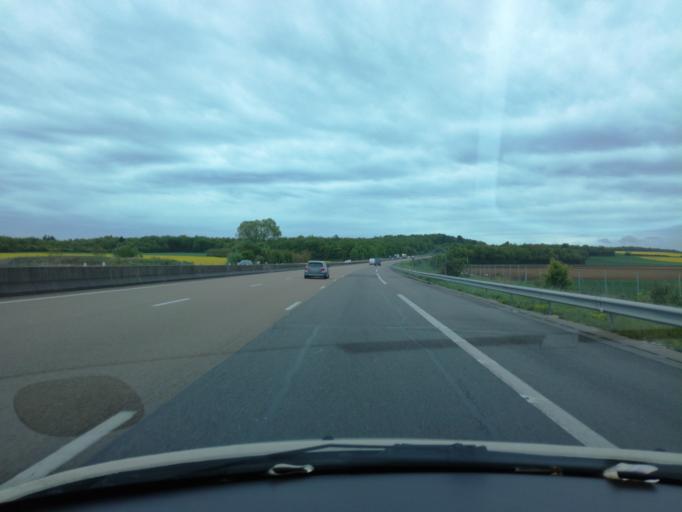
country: FR
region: Bourgogne
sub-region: Departement de la Cote-d'Or
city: Marcilly-sur-Tille
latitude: 47.4769
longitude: 5.1894
